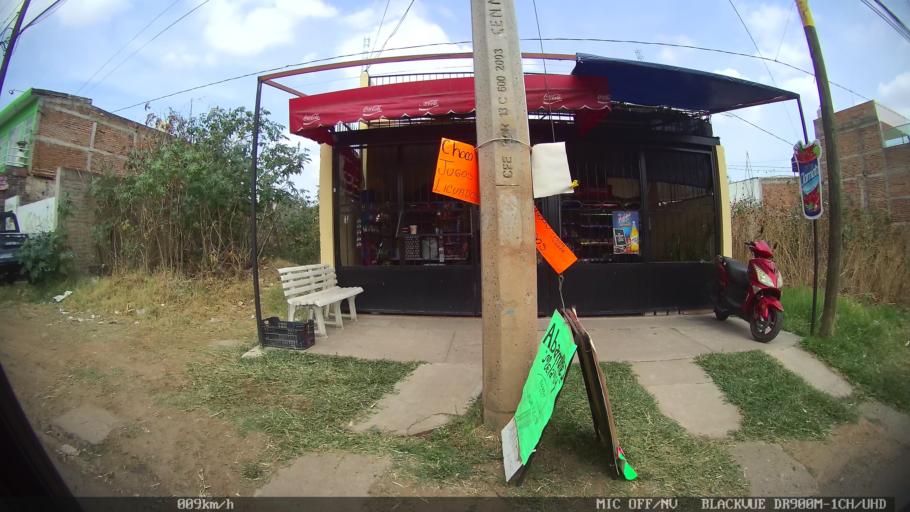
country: MX
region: Jalisco
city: Tonala
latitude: 20.6469
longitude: -103.2219
